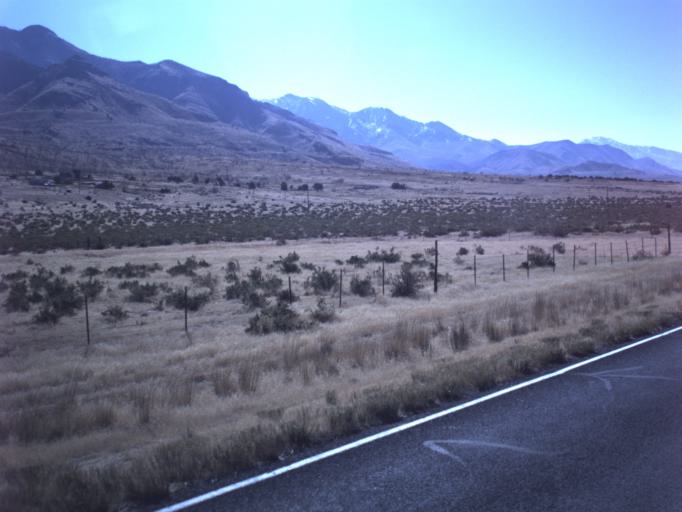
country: US
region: Utah
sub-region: Tooele County
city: Grantsville
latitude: 40.6812
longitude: -112.6711
